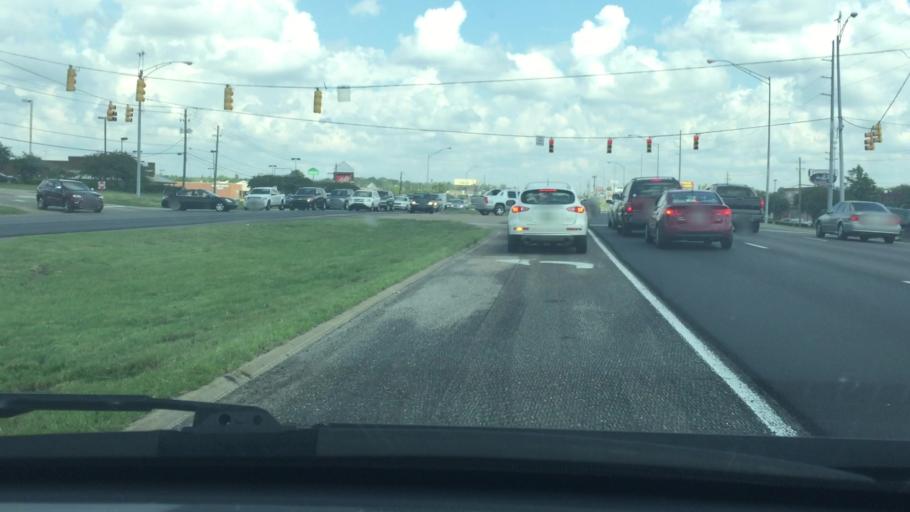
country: US
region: Alabama
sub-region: Montgomery County
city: Montgomery
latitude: 32.3478
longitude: -86.2219
